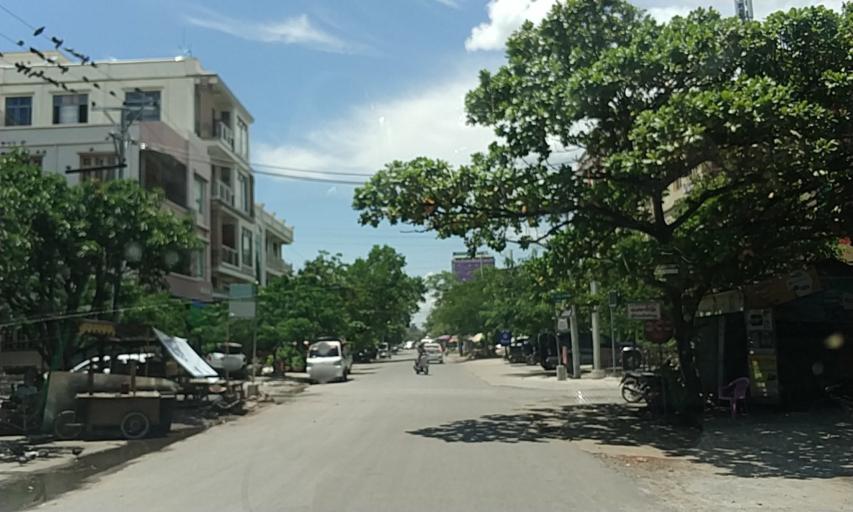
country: MM
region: Mandalay
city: Mandalay
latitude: 21.9738
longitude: 96.0966
